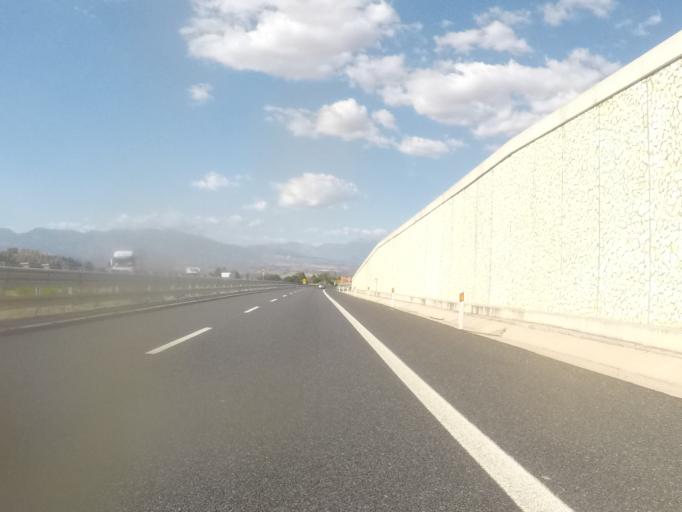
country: IT
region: Calabria
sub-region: Provincia di Cosenza
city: Tarsia
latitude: 39.6127
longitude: 16.2310
